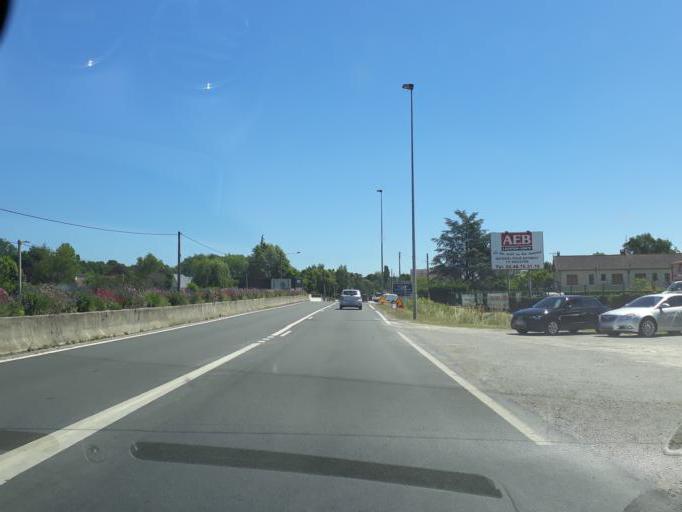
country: FR
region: Centre
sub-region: Departement du Cher
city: Vierzon
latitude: 47.2145
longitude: 2.1178
